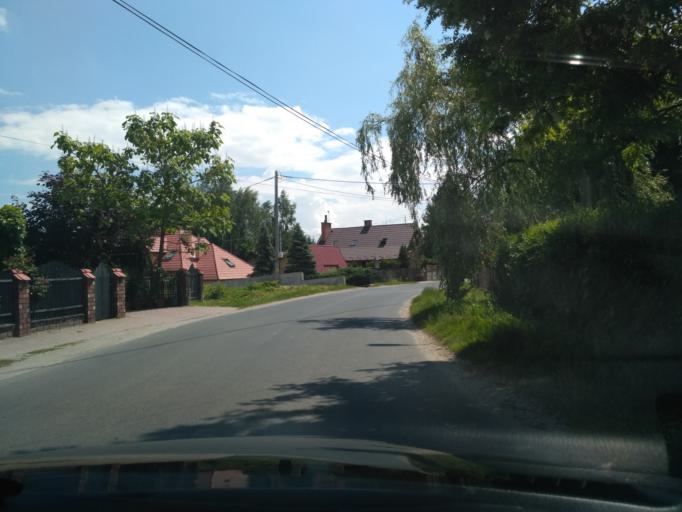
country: PL
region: Subcarpathian Voivodeship
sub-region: Powiat lancucki
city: Sonina
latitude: 50.0607
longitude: 22.2666
